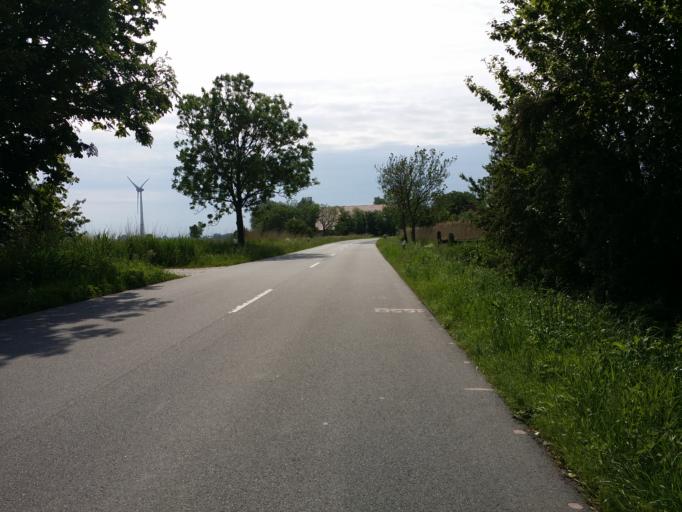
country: DE
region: Lower Saxony
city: Werdum
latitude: 53.6782
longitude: 7.7150
